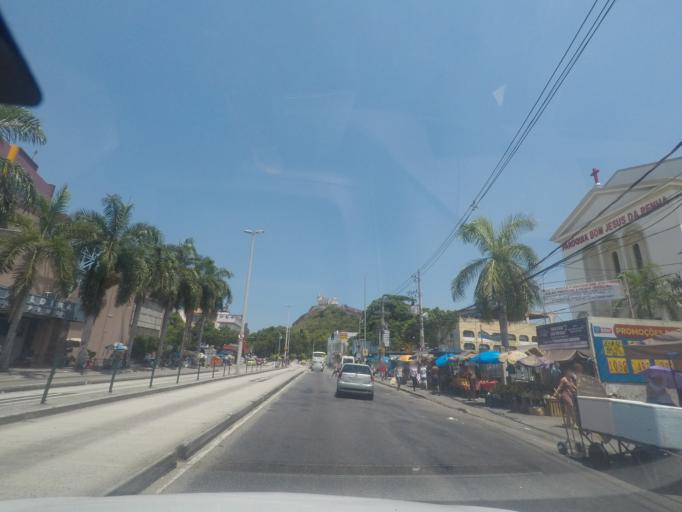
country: BR
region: Rio de Janeiro
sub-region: Duque De Caxias
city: Duque de Caxias
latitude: -22.8411
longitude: -43.2801
